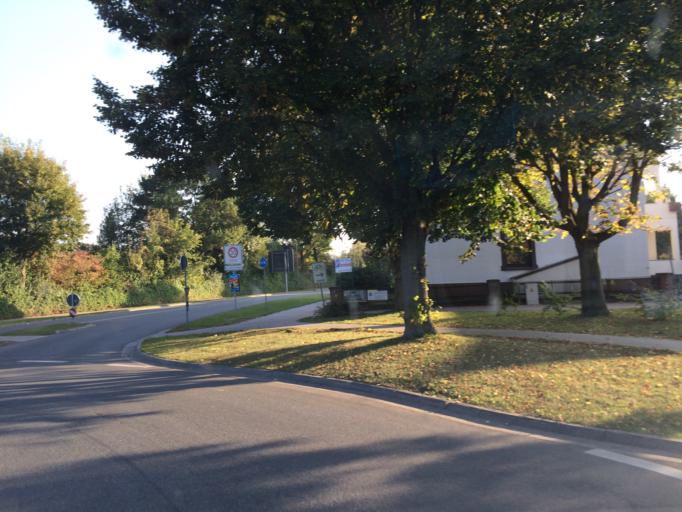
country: DE
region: Lower Saxony
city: Gehrden
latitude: 52.3196
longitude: 9.6000
